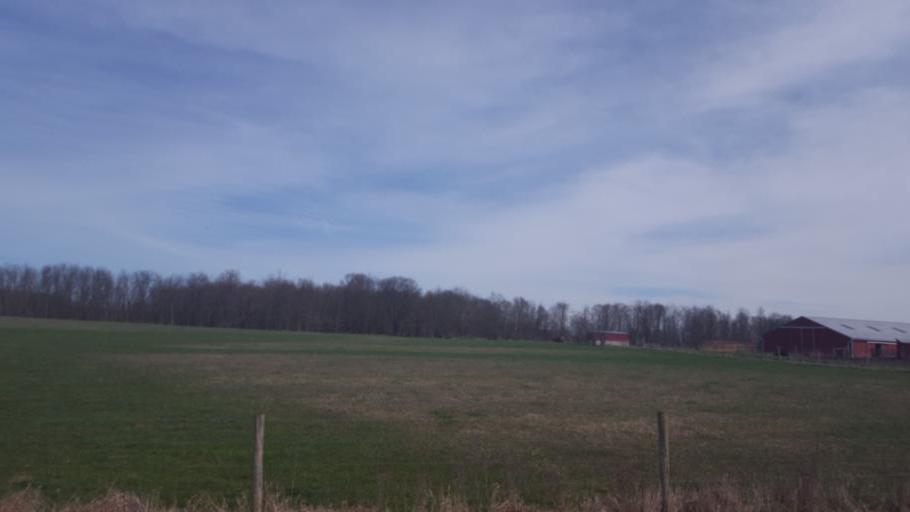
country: US
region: Michigan
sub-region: Gladwin County
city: Gladwin
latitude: 44.0458
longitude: -84.4674
